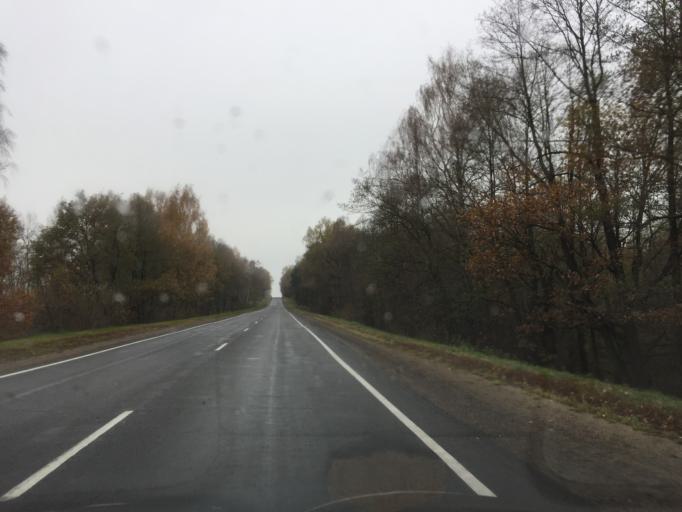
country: BY
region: Gomel
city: Karma
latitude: 53.3383
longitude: 30.7974
